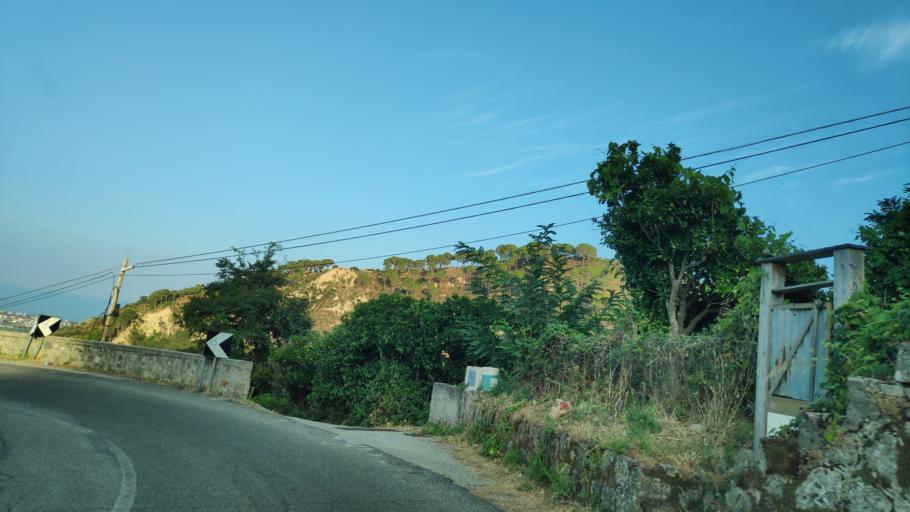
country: IT
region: Calabria
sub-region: Provincia di Catanzaro
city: Satriano
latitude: 38.6702
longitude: 16.4866
